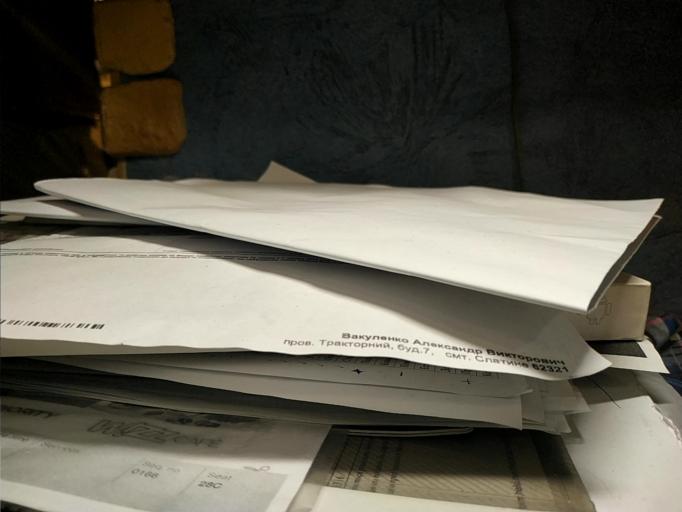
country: RU
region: Tverskaya
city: Zubtsov
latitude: 56.0994
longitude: 34.6924
